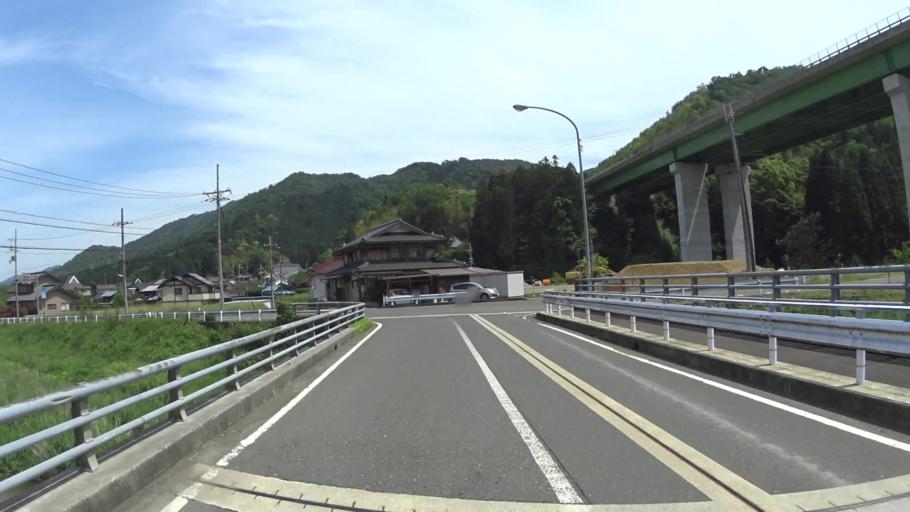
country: JP
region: Fukui
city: Obama
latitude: 35.4483
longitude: 135.5566
